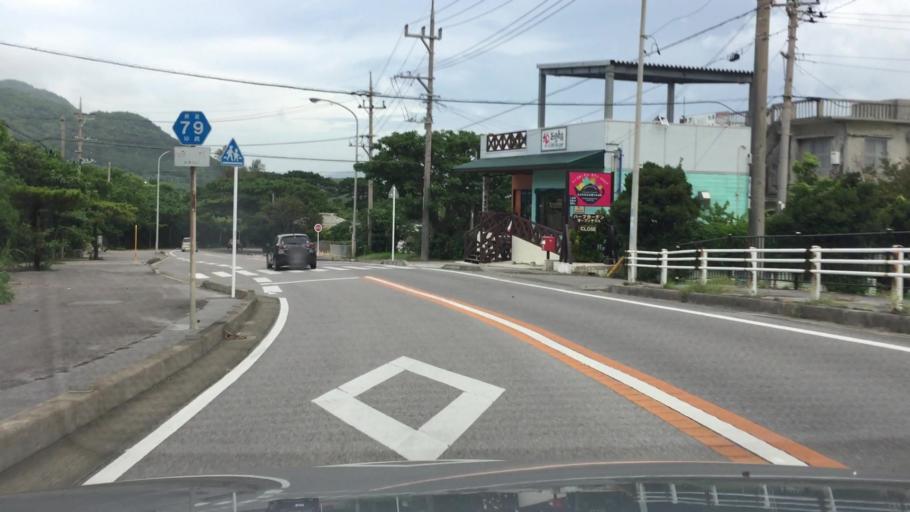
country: JP
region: Okinawa
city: Ishigaki
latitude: 24.4397
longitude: 124.1181
